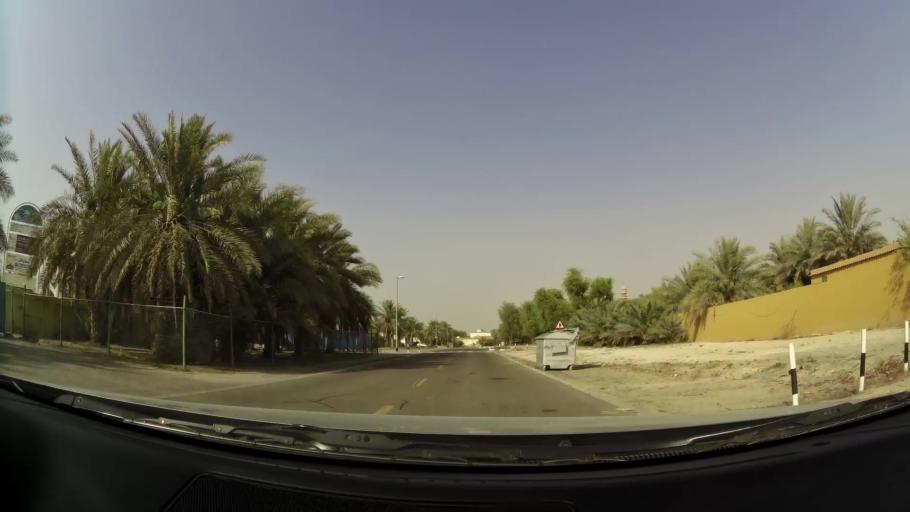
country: AE
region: Dubai
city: Dubai
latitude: 25.1476
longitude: 55.3232
